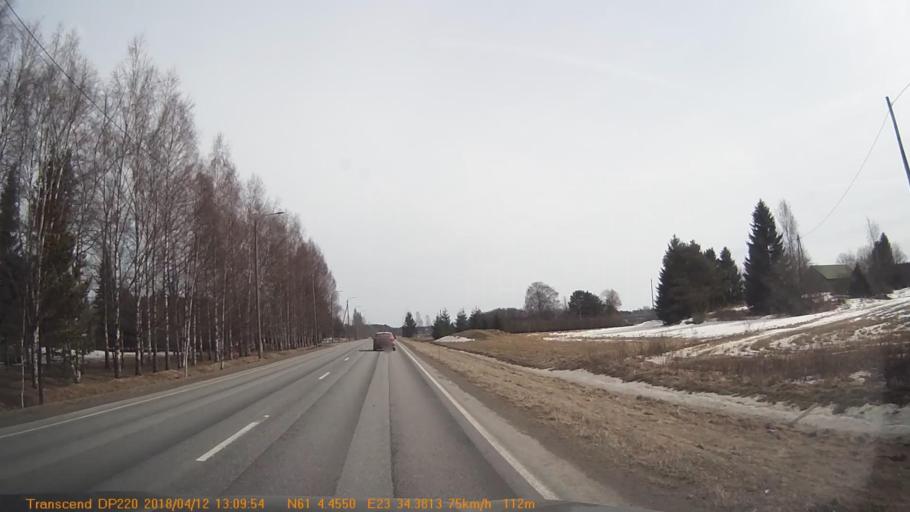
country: FI
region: Pirkanmaa
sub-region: Etelae-Pirkanmaa
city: Urjala
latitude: 61.0740
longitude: 23.5745
